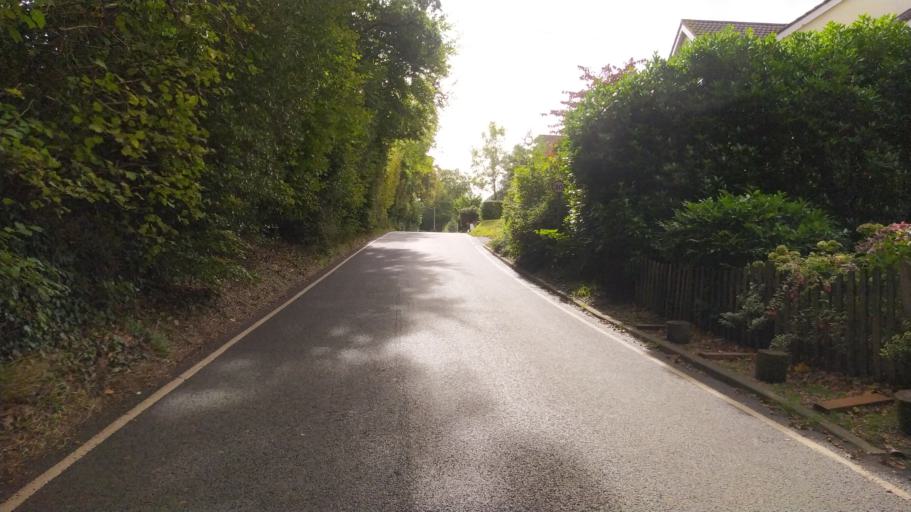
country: GB
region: England
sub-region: Hampshire
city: Romsey
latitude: 51.0194
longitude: -1.5431
